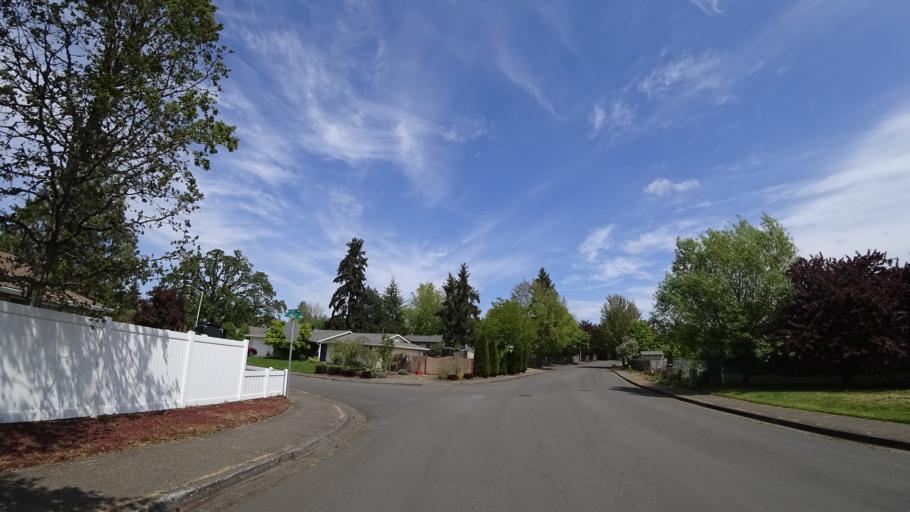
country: US
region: Oregon
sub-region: Washington County
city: Aloha
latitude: 45.4716
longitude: -122.8906
